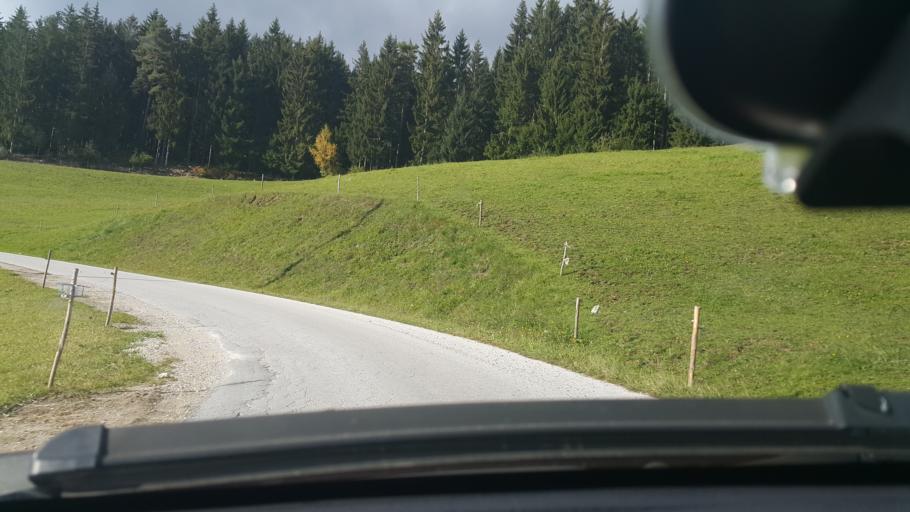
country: SI
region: Vitanje
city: Vitanje
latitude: 46.4097
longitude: 15.2841
